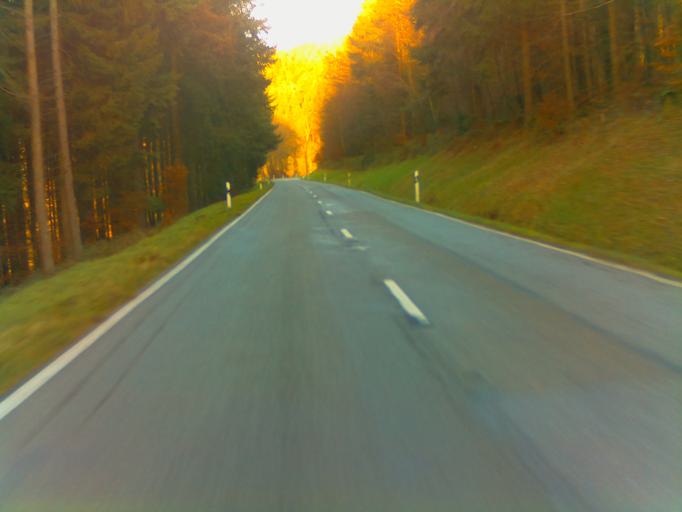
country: DE
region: Hesse
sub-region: Regierungsbezirk Darmstadt
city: Hesseneck
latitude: 49.5634
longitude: 9.1328
